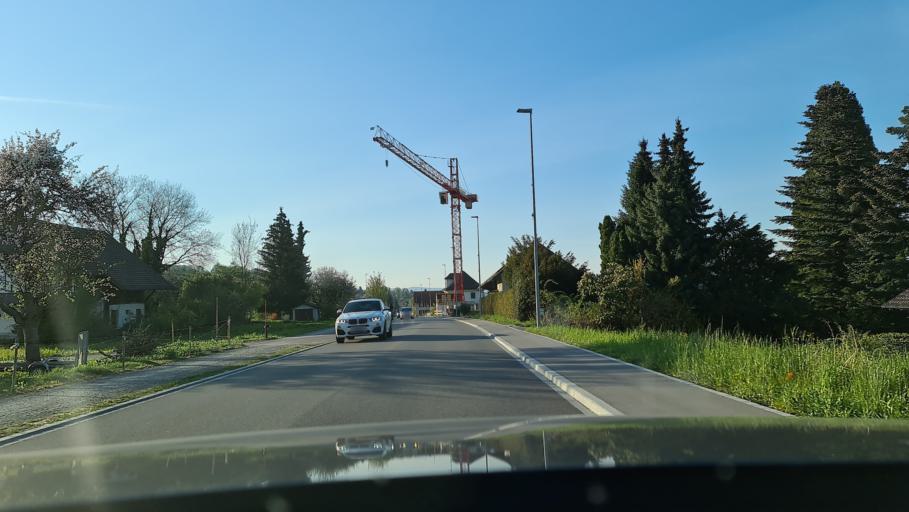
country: CH
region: Aargau
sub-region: Bezirk Lenzburg
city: Boniswil
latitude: 47.3100
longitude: 8.1907
